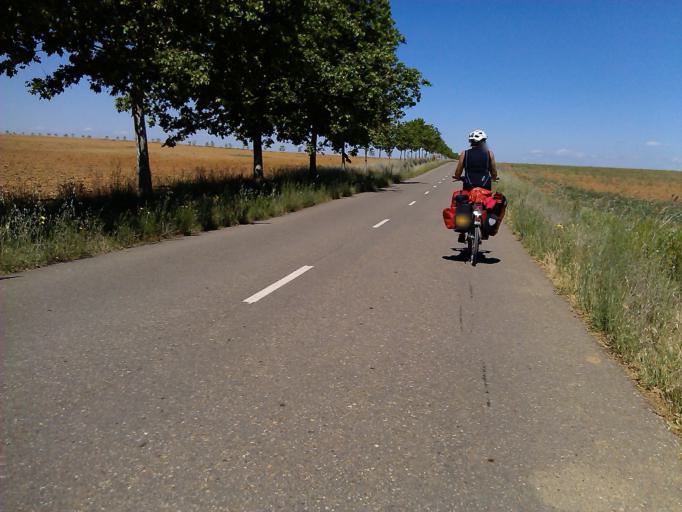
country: ES
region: Castille and Leon
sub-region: Provincia de Leon
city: Villamoratiel de las Matas
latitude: 42.4591
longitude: -5.2954
